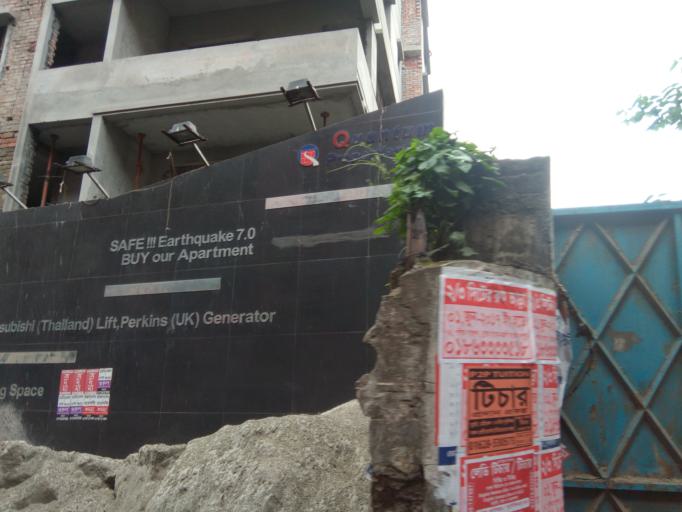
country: BD
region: Dhaka
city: Azimpur
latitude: 23.7574
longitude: 90.3845
